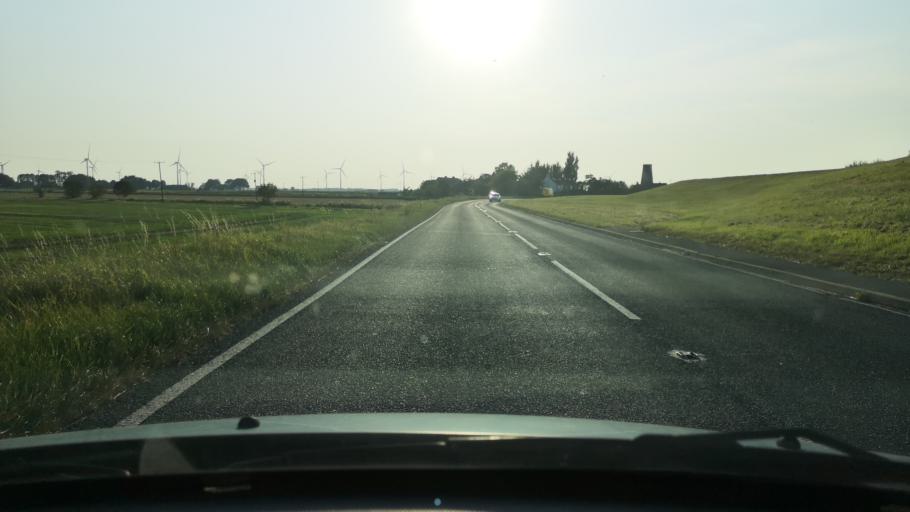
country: GB
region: England
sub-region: East Riding of Yorkshire
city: Skelton
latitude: 53.6834
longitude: -0.8496
